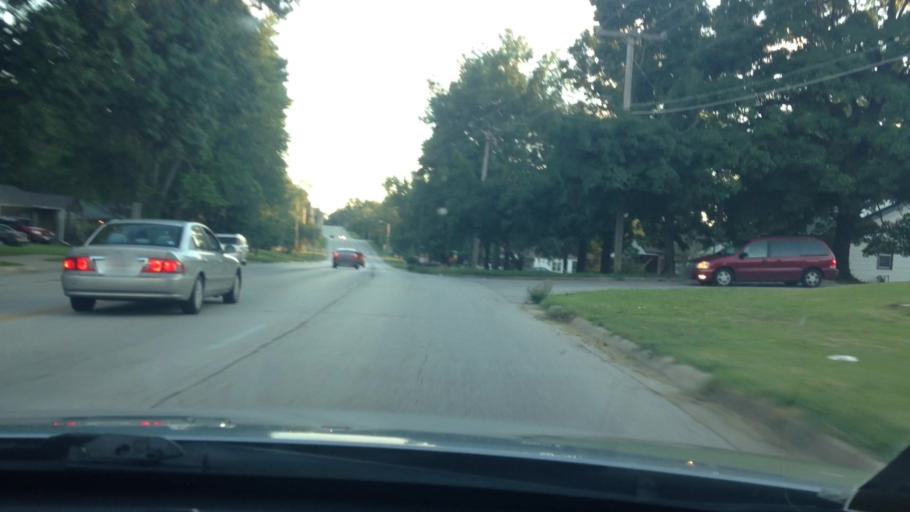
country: US
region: Missouri
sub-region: Jackson County
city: Raytown
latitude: 38.9904
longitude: -94.4827
